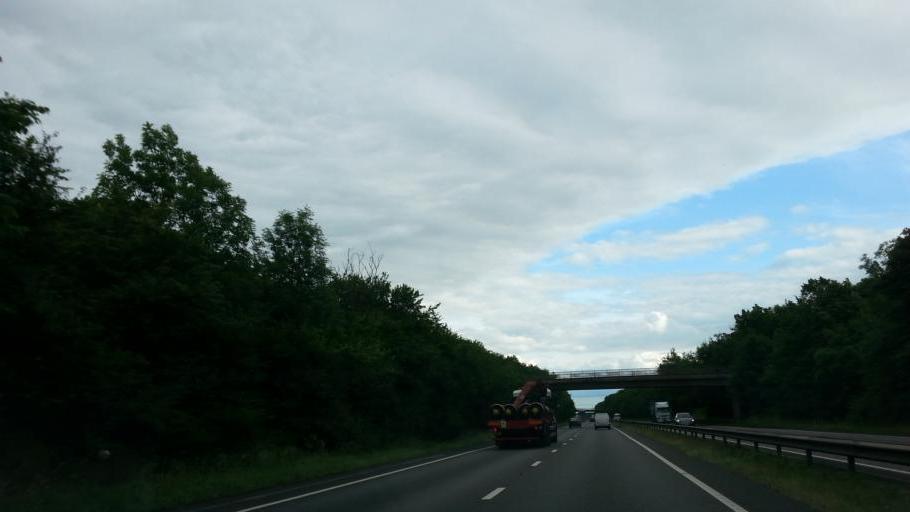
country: GB
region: England
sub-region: Nottinghamshire
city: Tuxford
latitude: 53.2085
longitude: -0.8692
